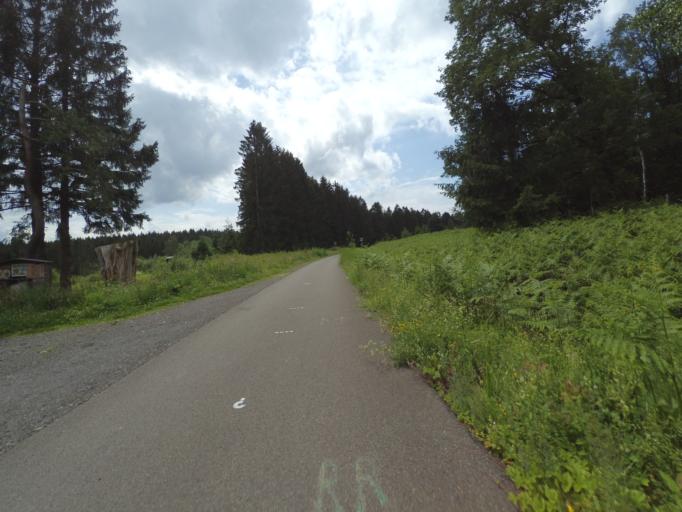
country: BE
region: Wallonia
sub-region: Province de Liege
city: Raeren
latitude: 50.6584
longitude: 6.1270
